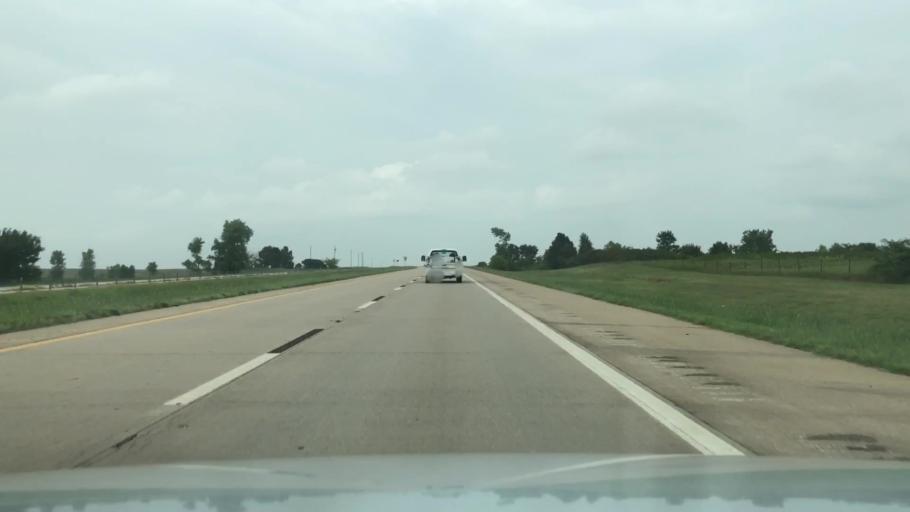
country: US
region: Oklahoma
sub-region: Osage County
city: Skiatook
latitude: 36.4141
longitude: -95.9203
